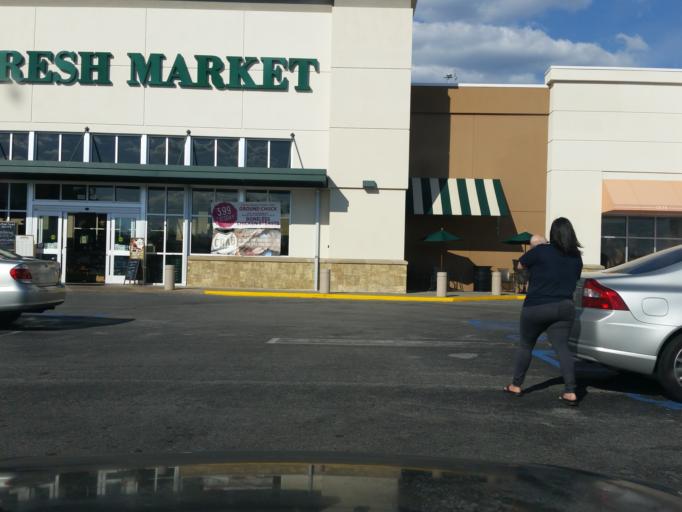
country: US
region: Florida
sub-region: Escambia County
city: Ferry Pass
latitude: 30.4812
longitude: -87.2081
